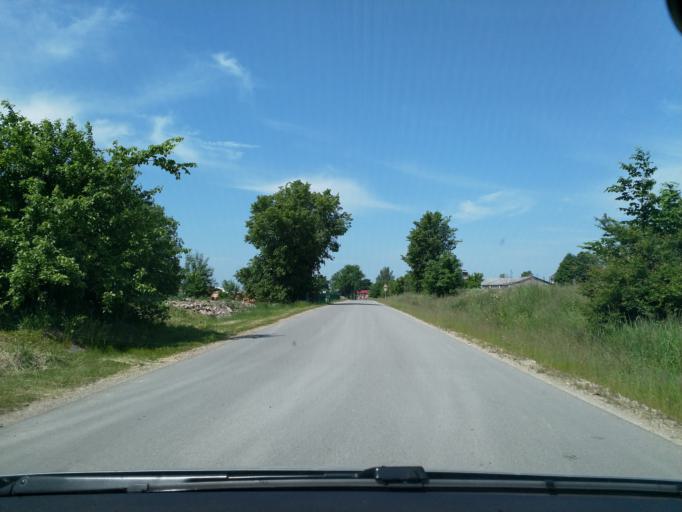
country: LV
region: Kuldigas Rajons
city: Kuldiga
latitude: 56.9575
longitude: 22.0123
